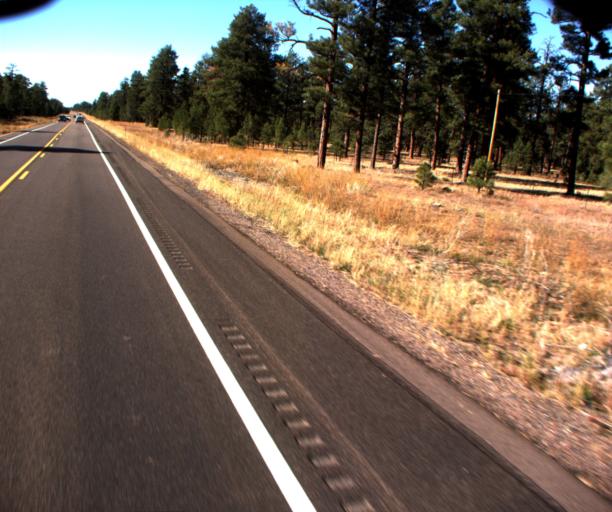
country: US
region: Arizona
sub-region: Apache County
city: Saint Michaels
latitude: 35.6940
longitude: -109.2674
